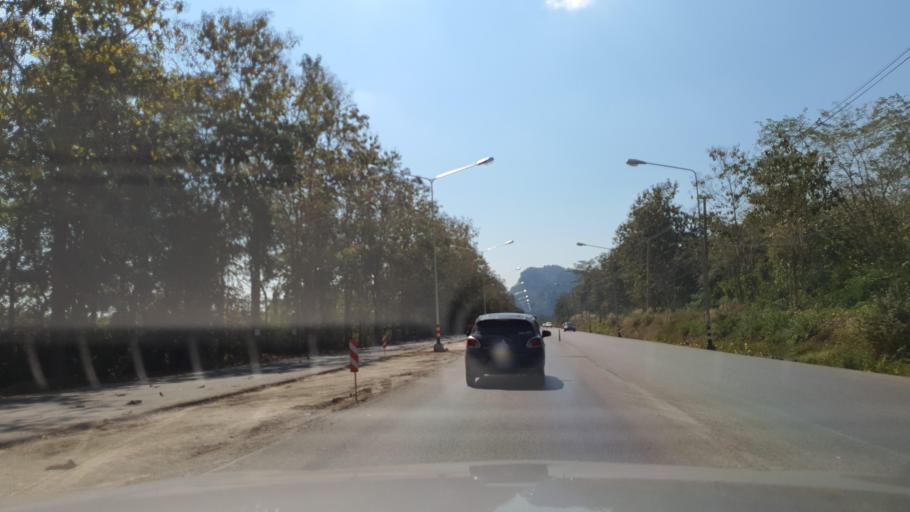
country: TH
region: Nan
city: Nan
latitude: 18.8735
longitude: 100.7437
